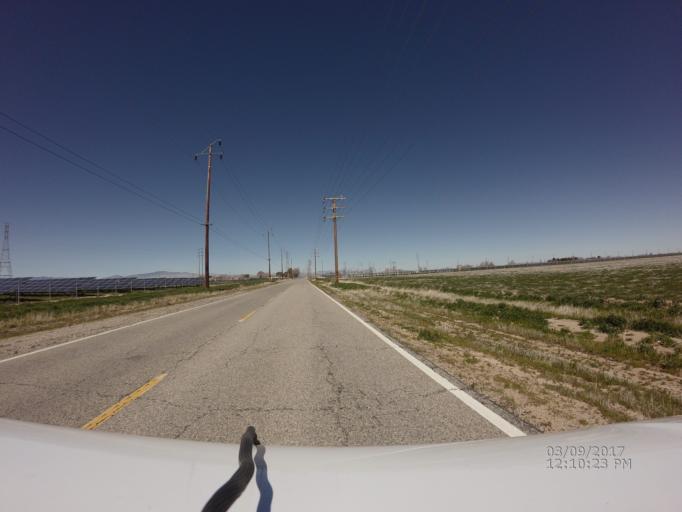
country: US
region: California
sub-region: Los Angeles County
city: Leona Valley
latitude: 34.7138
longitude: -118.2894
